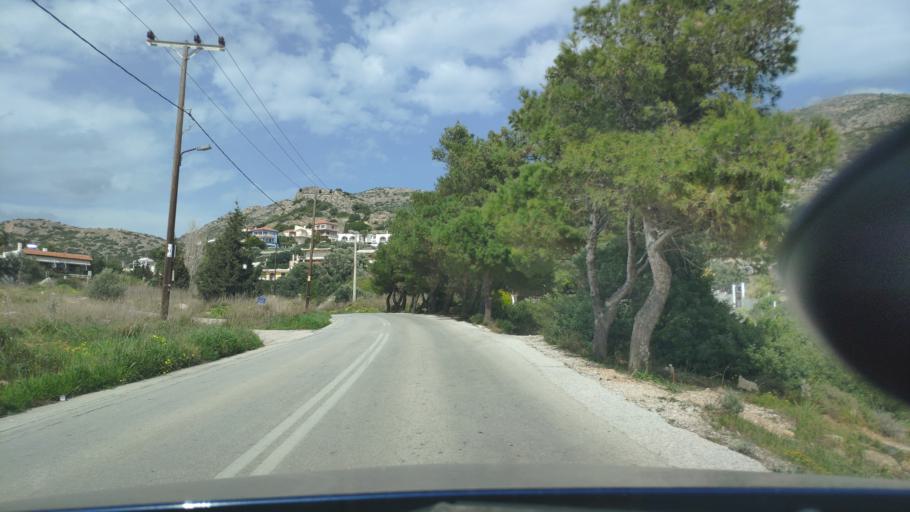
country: GR
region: Attica
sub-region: Nomarchia Anatolikis Attikis
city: Limin Mesoyaias
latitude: 37.8983
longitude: 24.0240
